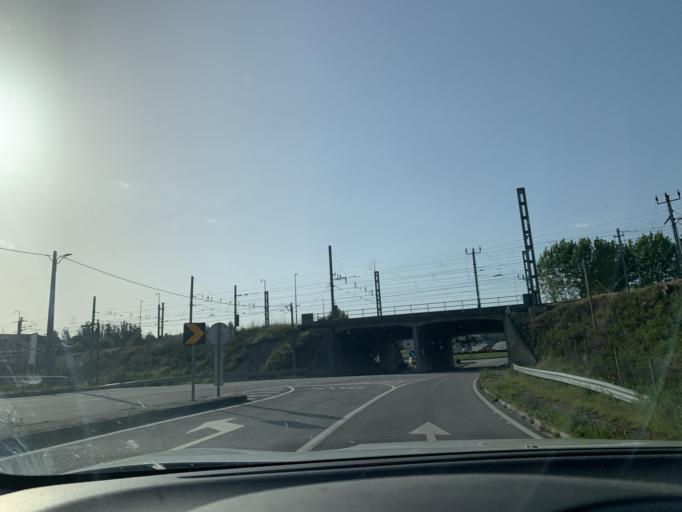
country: PT
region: Viseu
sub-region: Mangualde
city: Mangualde
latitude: 40.5847
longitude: -7.7619
